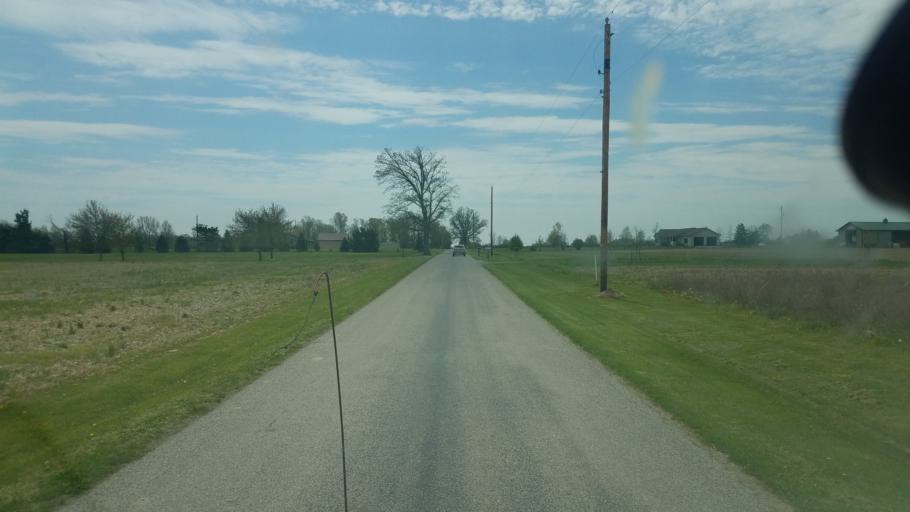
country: US
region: Ohio
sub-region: Allen County
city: Bluffton
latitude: 40.8049
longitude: -83.9087
